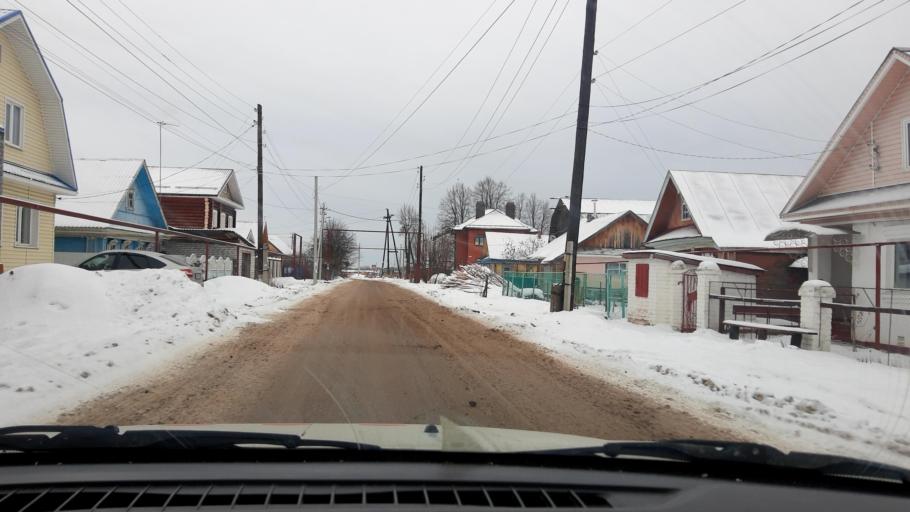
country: RU
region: Nizjnij Novgorod
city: Gorodets
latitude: 56.6668
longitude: 43.4776
